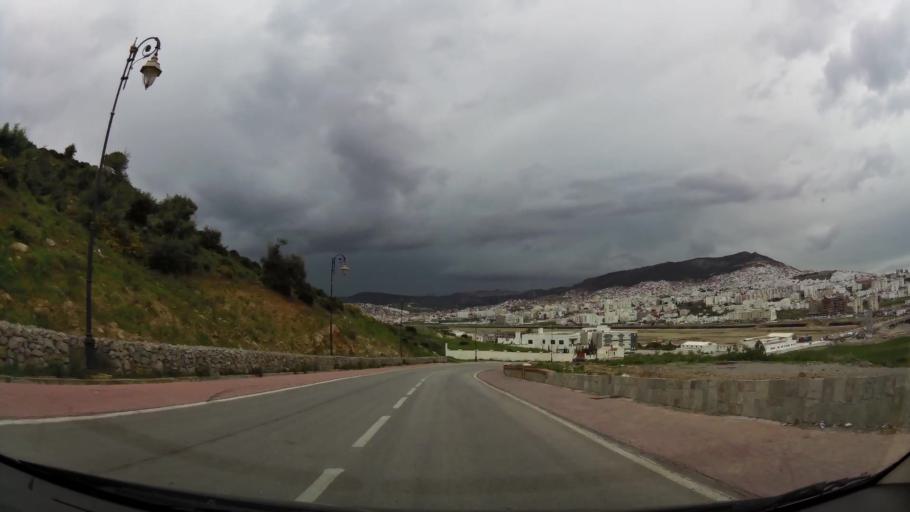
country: MA
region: Tanger-Tetouan
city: Tetouan
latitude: 35.5544
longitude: -5.3746
